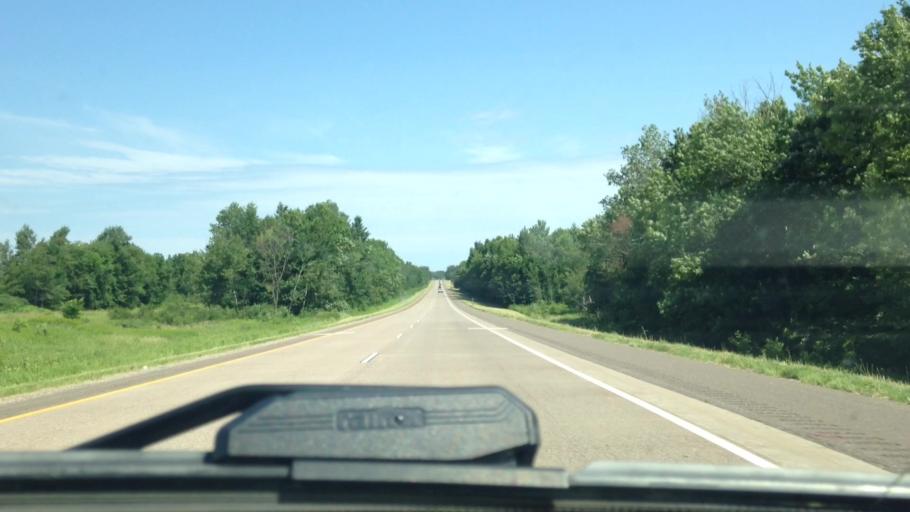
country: US
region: Wisconsin
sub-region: Barron County
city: Rice Lake
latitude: 45.5394
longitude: -91.7612
